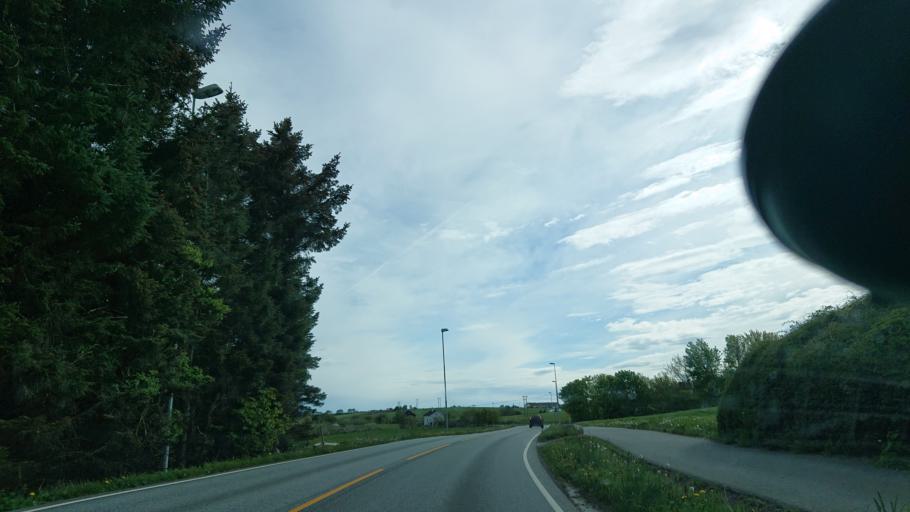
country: NO
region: Rogaland
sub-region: Sola
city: Tananger
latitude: 58.9480
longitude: 5.6006
